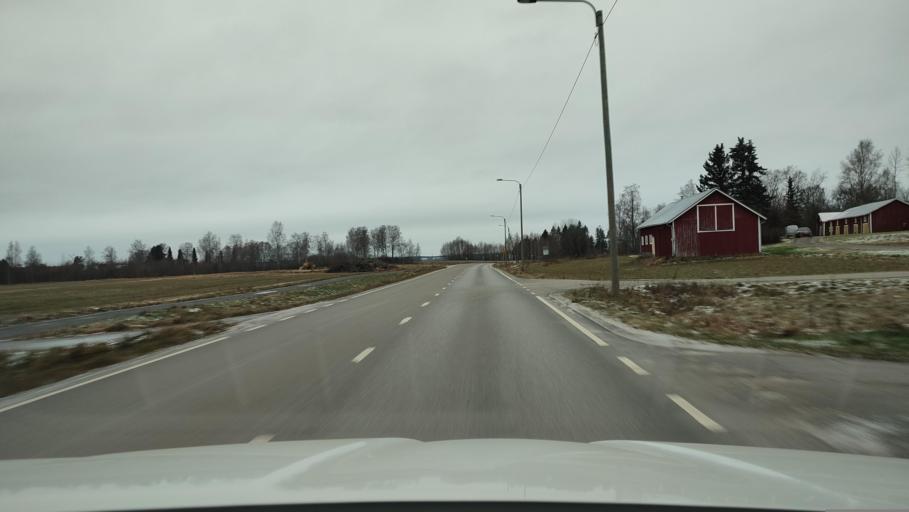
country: FI
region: Ostrobothnia
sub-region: Vaasa
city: Ristinummi
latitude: 63.0350
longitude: 21.7876
